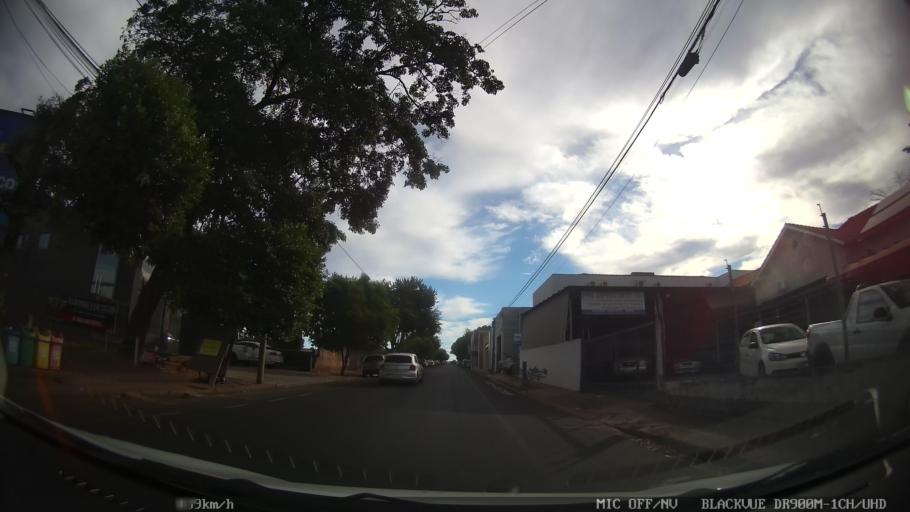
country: BR
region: Sao Paulo
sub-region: Catanduva
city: Catanduva
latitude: -21.1244
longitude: -48.9674
